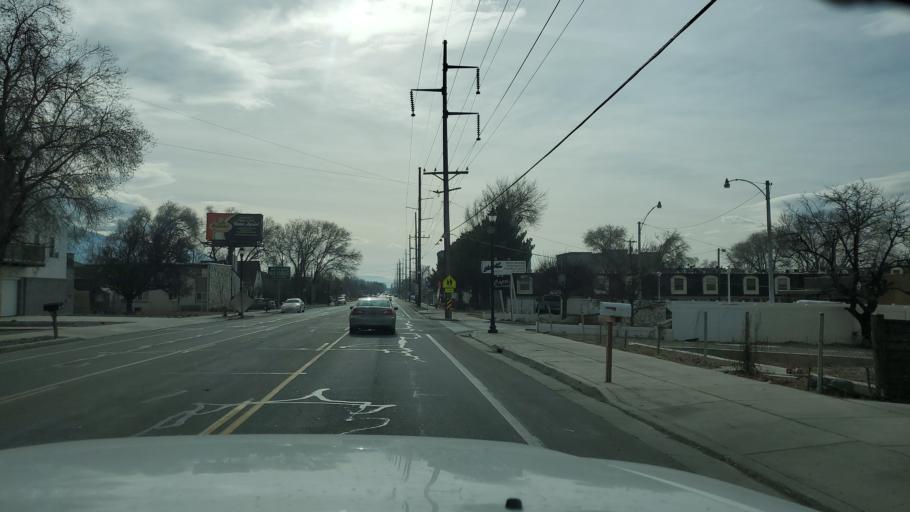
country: US
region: Utah
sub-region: Salt Lake County
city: Millcreek
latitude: 40.6938
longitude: -111.8655
